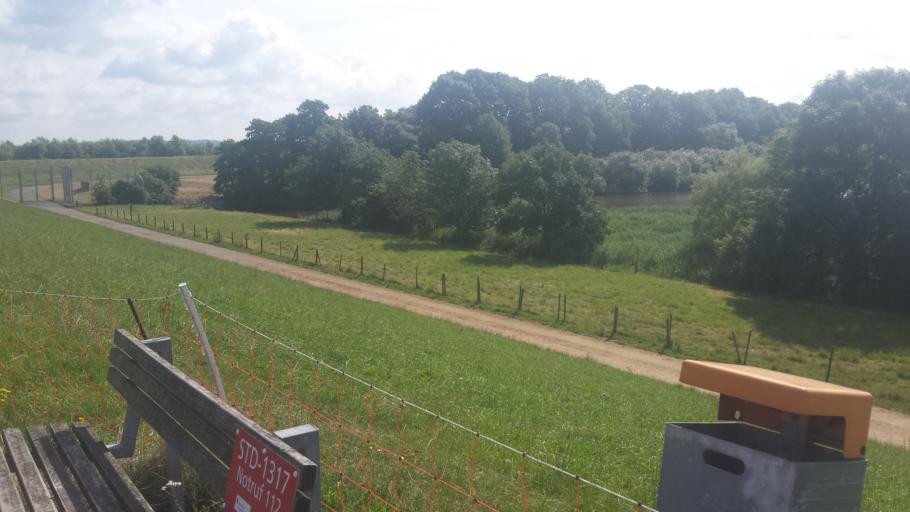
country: DE
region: Lower Saxony
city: Jork
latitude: 53.5474
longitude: 9.6892
